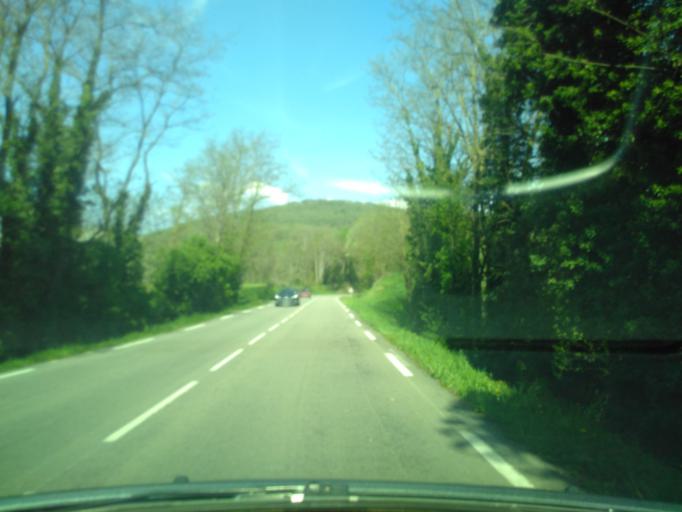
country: FR
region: Rhone-Alpes
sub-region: Departement de la Drome
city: Crest
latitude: 44.7000
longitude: 5.0060
